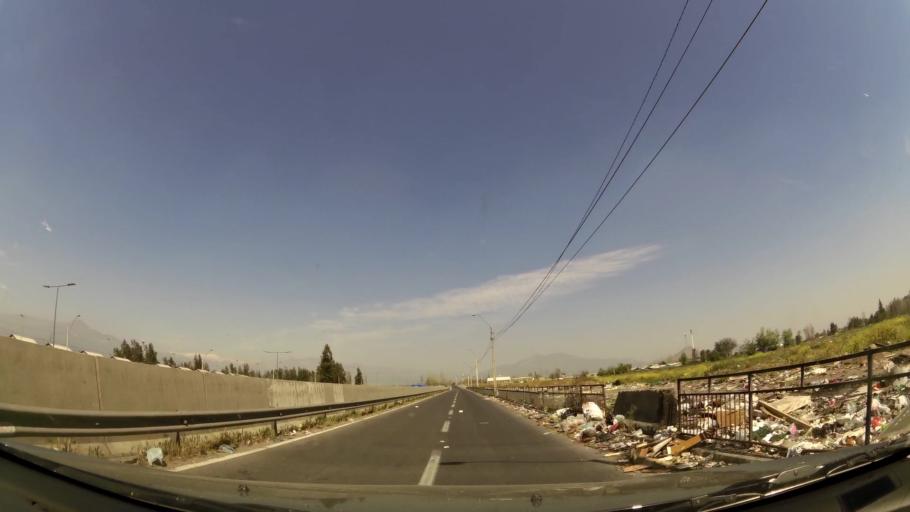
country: CL
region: Santiago Metropolitan
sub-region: Provincia de Santiago
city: La Pintana
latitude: -33.5951
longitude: -70.6076
